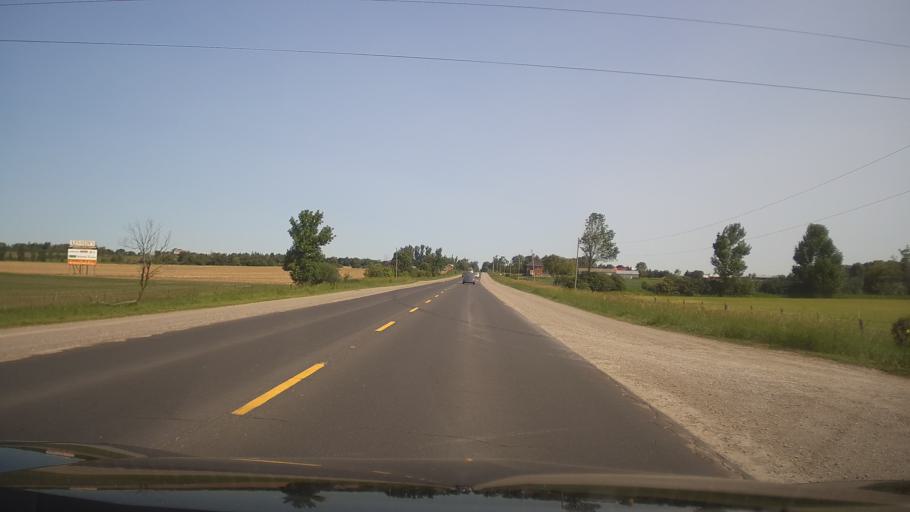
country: CA
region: Ontario
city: Omemee
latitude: 44.3248
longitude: -78.6848
